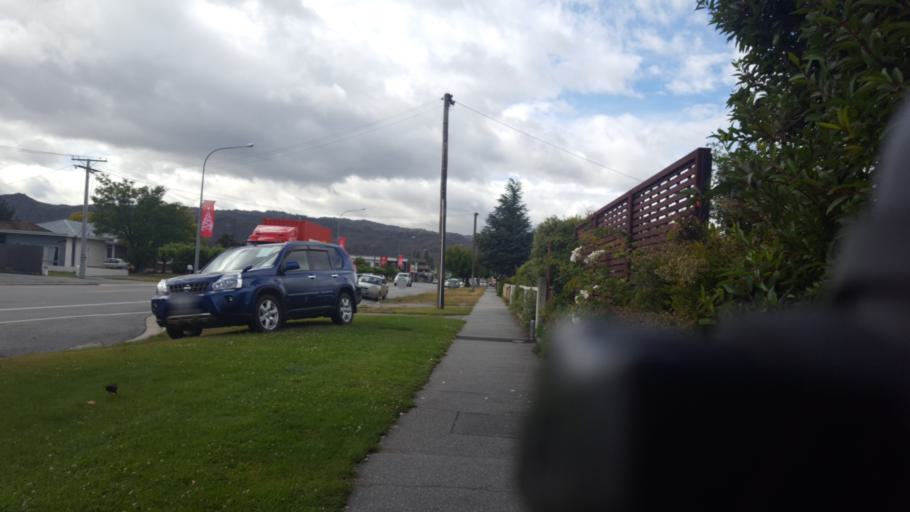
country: NZ
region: Otago
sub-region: Queenstown-Lakes District
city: Wanaka
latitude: -45.2485
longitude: 169.3848
